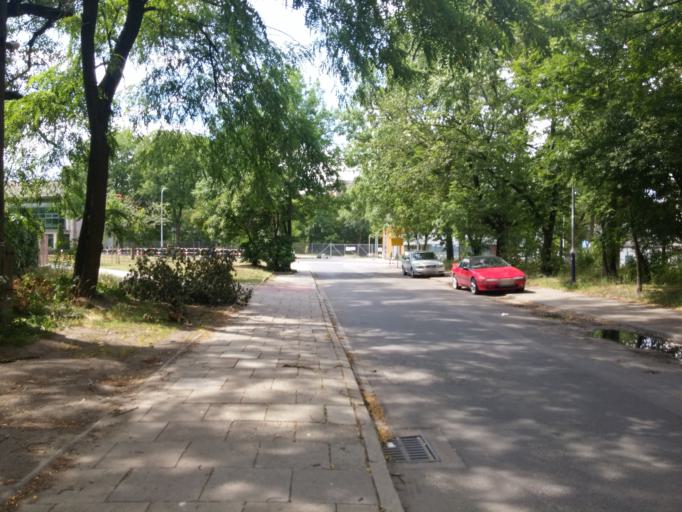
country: PL
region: Lesser Poland Voivodeship
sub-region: Krakow
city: Krakow
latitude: 50.0461
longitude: 19.9673
